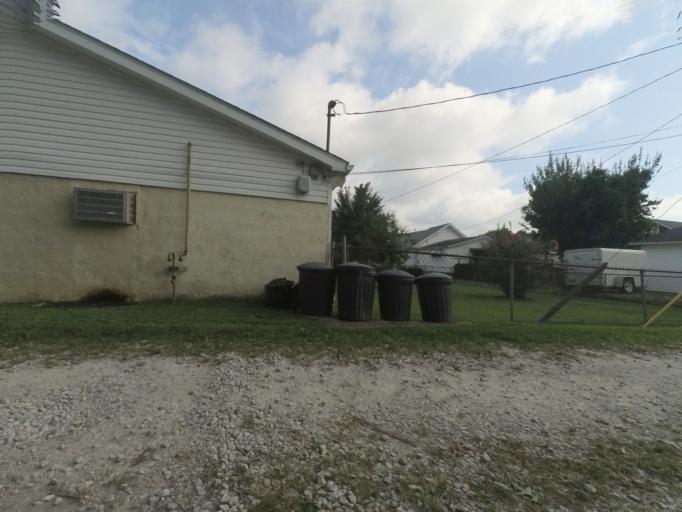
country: US
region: West Virginia
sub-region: Cabell County
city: Huntington
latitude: 38.4336
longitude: -82.4032
